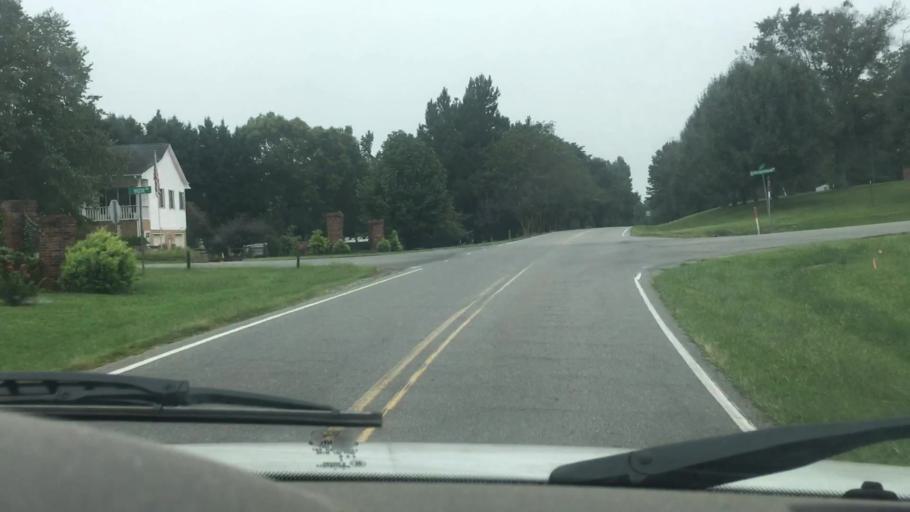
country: US
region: North Carolina
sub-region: Gaston County
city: Davidson
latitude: 35.5208
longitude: -80.7986
